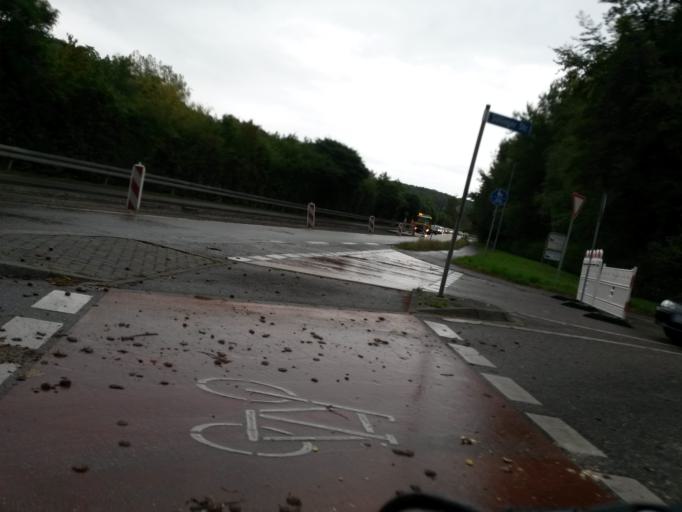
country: DE
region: Baden-Wuerttemberg
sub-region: Karlsruhe Region
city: Konigsbach-Stein
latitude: 48.9703
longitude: 8.5500
